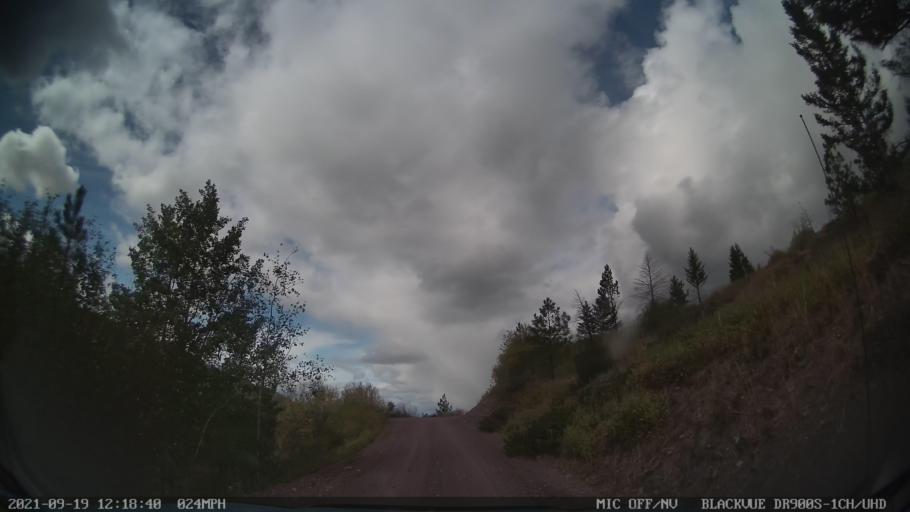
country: US
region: Montana
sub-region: Missoula County
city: Seeley Lake
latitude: 47.1763
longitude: -113.3669
